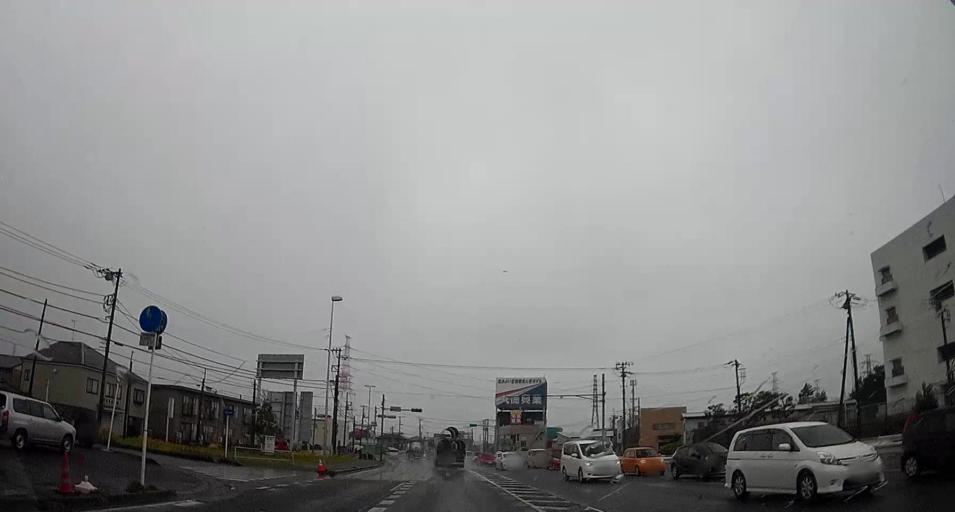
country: JP
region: Chiba
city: Chiba
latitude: 35.5695
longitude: 140.1294
